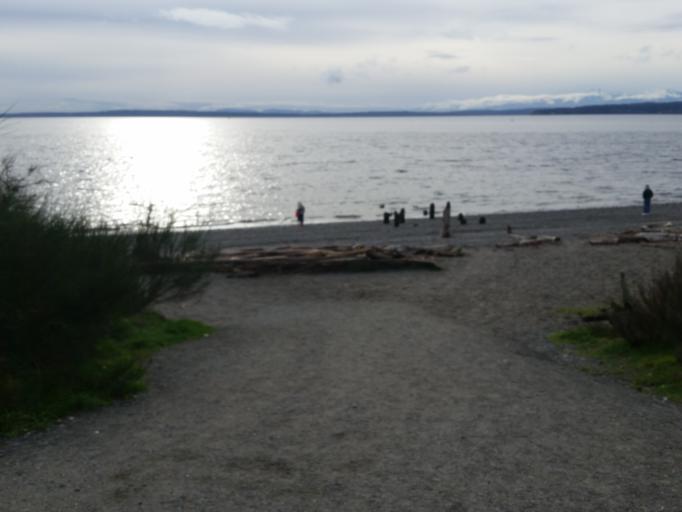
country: US
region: Washington
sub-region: Snohomish County
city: Woodway
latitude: 47.7637
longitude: -122.3856
